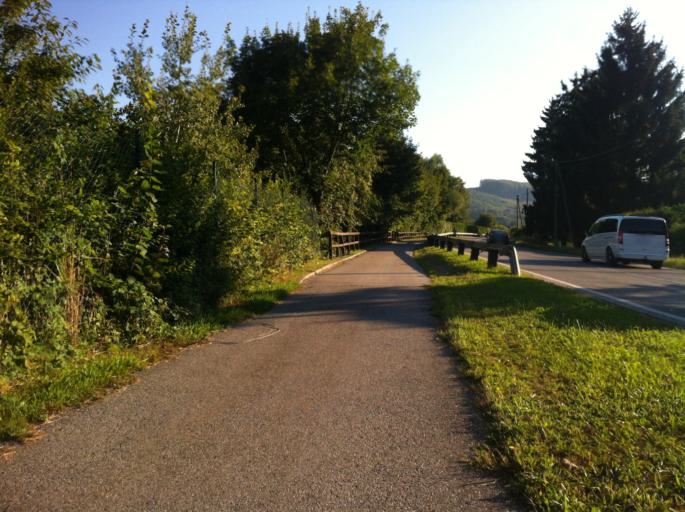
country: AT
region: Lower Austria
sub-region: Politischer Bezirk Wien-Umgebung
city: Wolfsgraben
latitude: 48.1851
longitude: 16.1227
